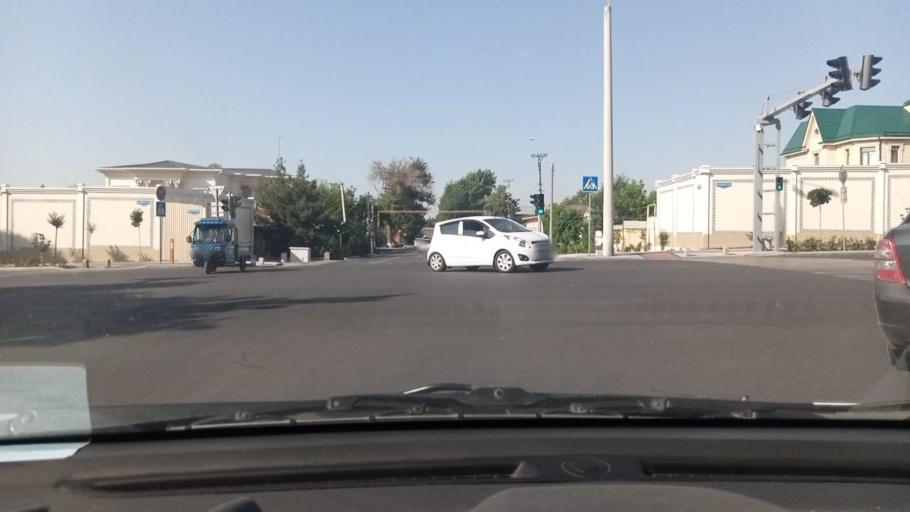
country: UZ
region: Toshkent
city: Salor
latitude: 41.3292
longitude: 69.3549
